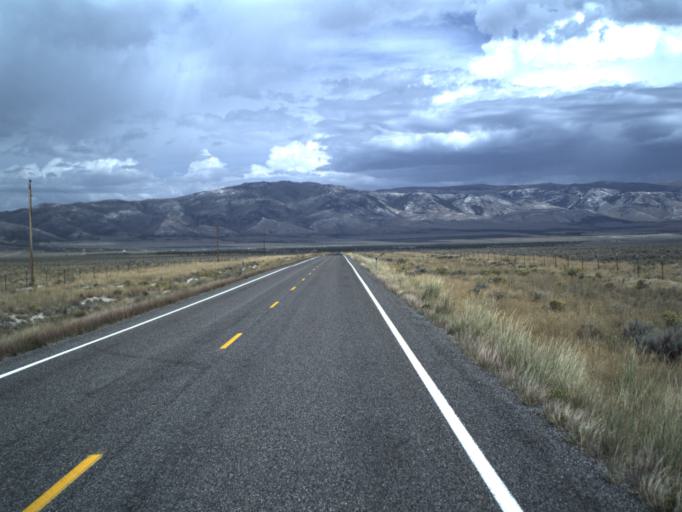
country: US
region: Idaho
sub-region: Cassia County
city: Burley
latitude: 41.7459
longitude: -113.5175
